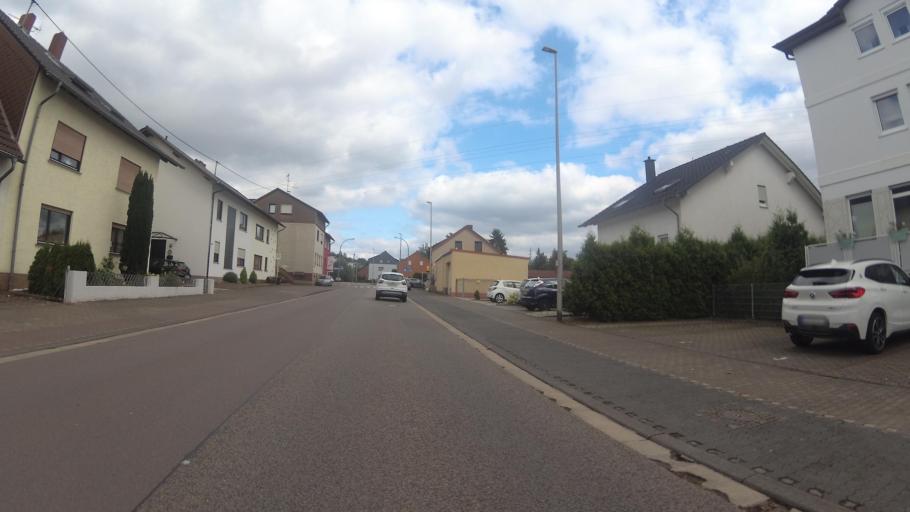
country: DE
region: Saarland
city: Puttlingen
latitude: 49.2578
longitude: 6.8874
